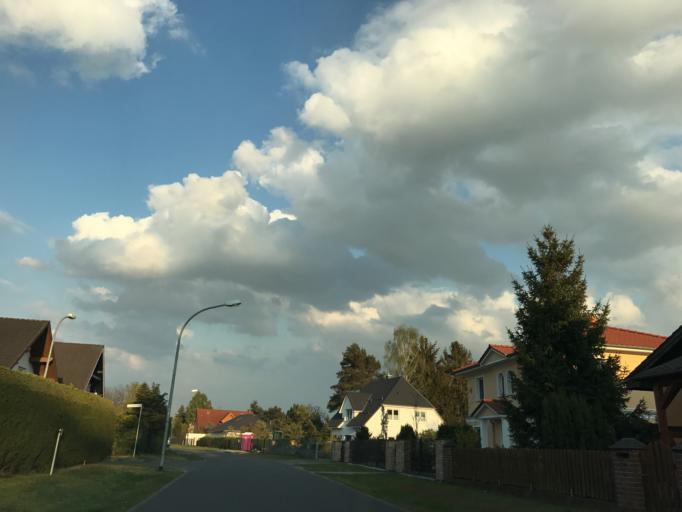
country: DE
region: Brandenburg
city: Falkensee
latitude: 52.5485
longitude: 13.0824
